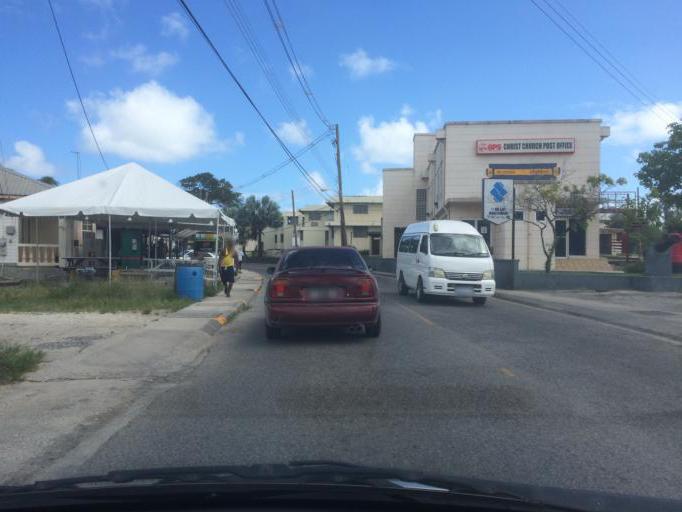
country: BB
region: Christ Church
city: Oistins
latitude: 13.0628
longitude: -59.5414
